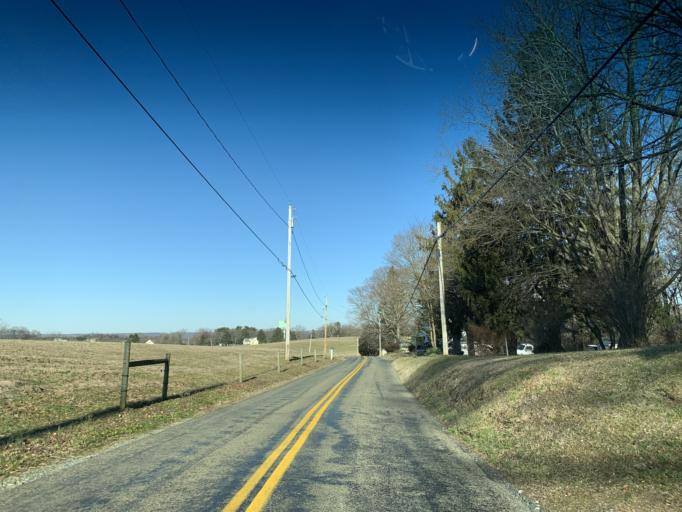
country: US
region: Maryland
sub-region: Harford County
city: Aberdeen
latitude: 39.5845
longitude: -76.2028
